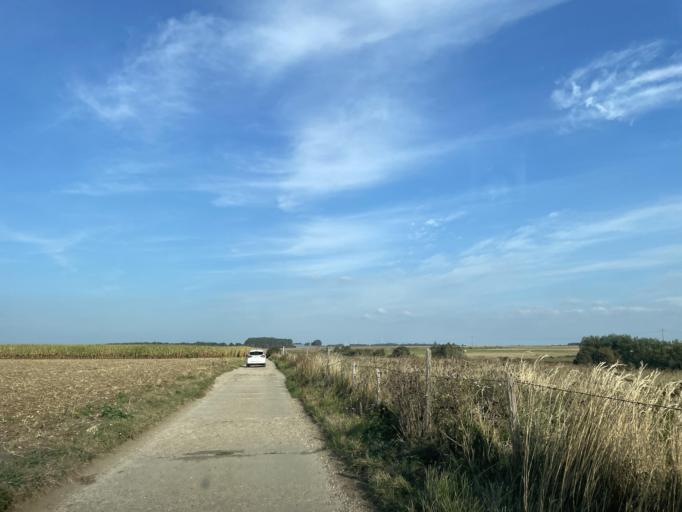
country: FR
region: Picardie
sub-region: Departement de la Somme
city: Mers-les-Bains
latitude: 50.0735
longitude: 1.3953
